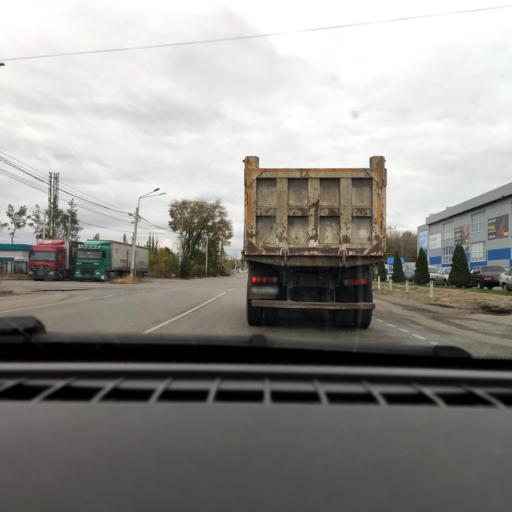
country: RU
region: Voronezj
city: Maslovka
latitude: 51.6366
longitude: 39.2911
